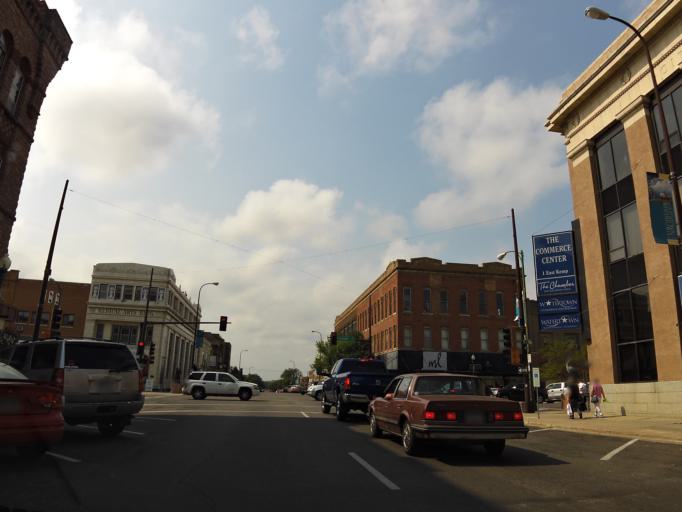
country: US
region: South Dakota
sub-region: Codington County
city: Watertown
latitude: 44.9004
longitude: -97.1141
